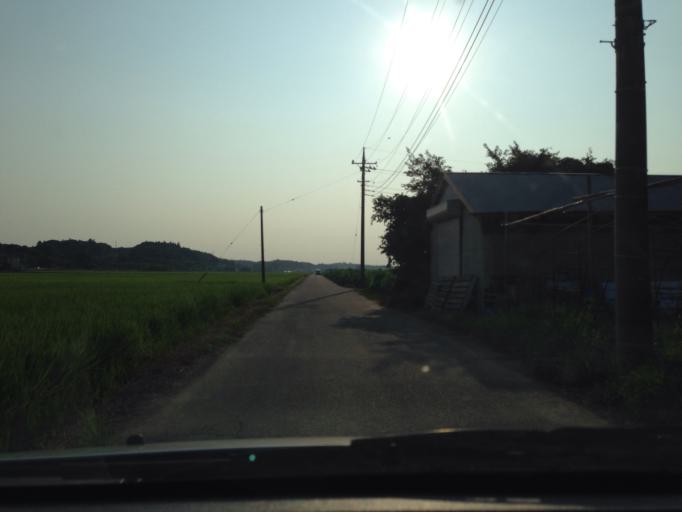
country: JP
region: Ibaraki
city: Ami
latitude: 36.0330
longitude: 140.2734
